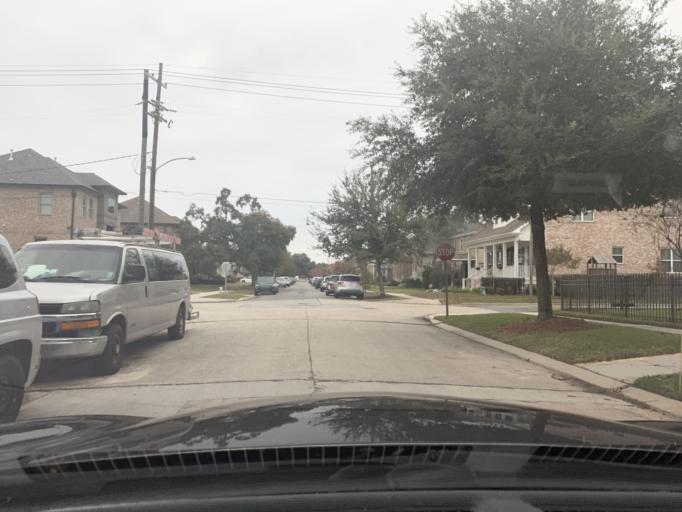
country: US
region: Louisiana
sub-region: Jefferson Parish
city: Metairie
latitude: 30.0158
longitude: -90.1080
